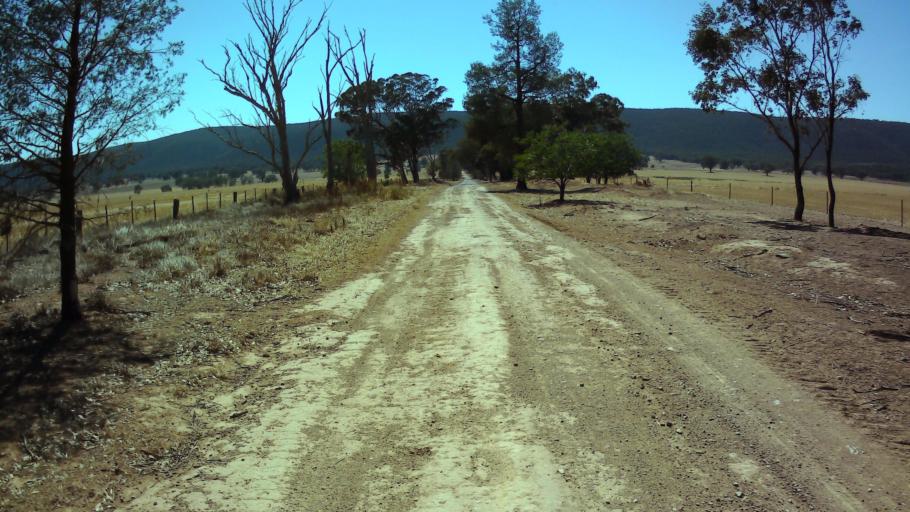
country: AU
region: New South Wales
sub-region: Weddin
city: Grenfell
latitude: -33.7024
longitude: 148.3264
